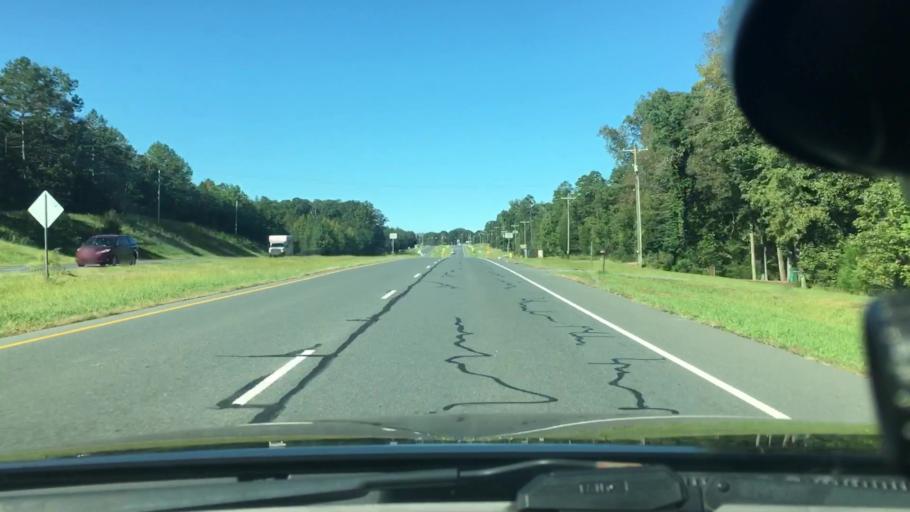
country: US
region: North Carolina
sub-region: Stanly County
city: Oakboro
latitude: 35.2694
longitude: -80.3371
